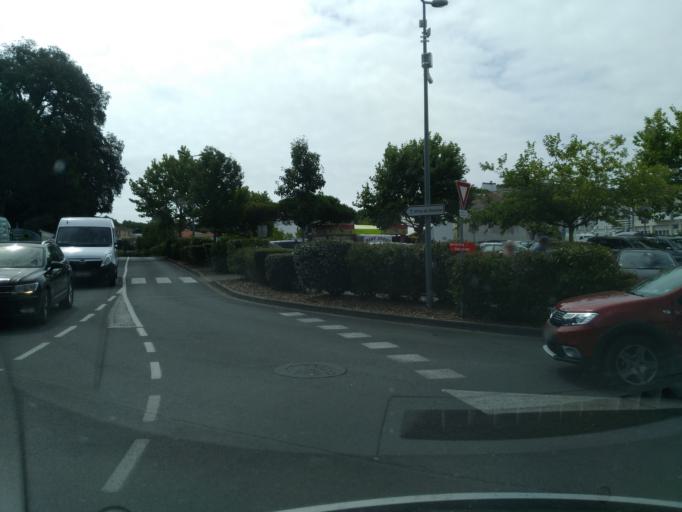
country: FR
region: Poitou-Charentes
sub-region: Departement de la Charente-Maritime
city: Saint-Palais-sur-Mer
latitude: 45.6446
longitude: -1.0884
